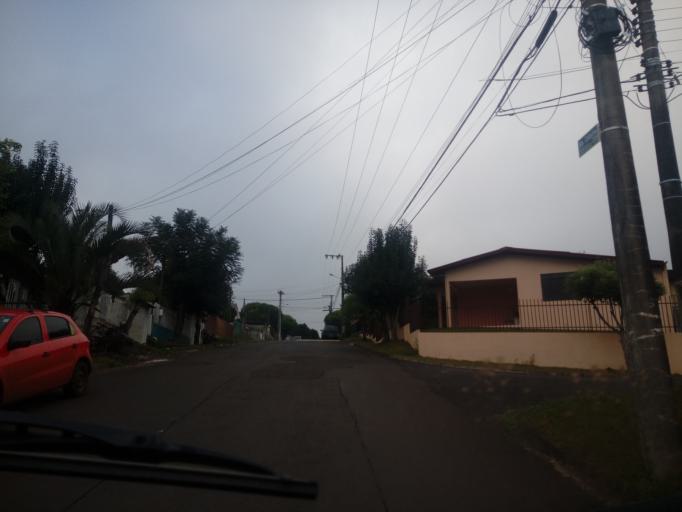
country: BR
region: Santa Catarina
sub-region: Chapeco
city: Chapeco
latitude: -27.1146
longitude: -52.6244
